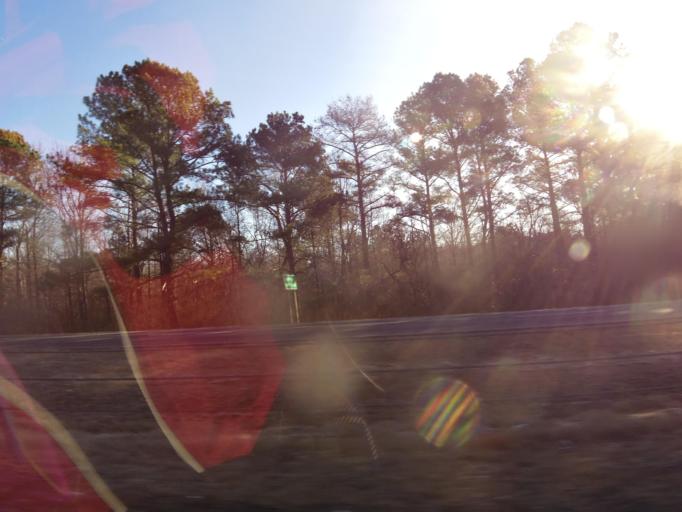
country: US
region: Alabama
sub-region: Cullman County
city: Good Hope
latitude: 34.0684
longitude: -86.8665
